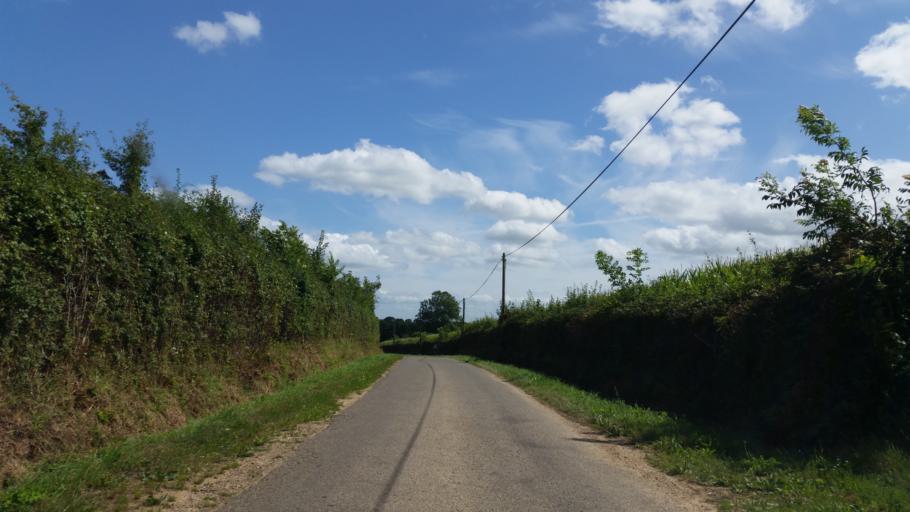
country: FR
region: Lower Normandy
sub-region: Departement de la Manche
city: Sainte-Mere-Eglise
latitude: 49.4609
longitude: -1.3291
